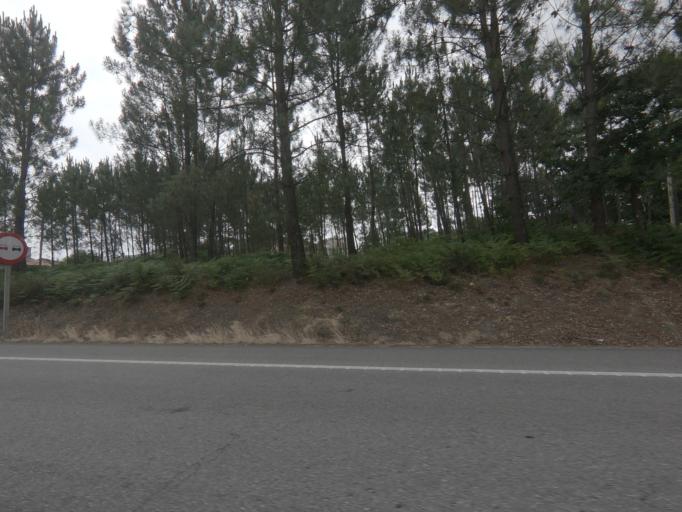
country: PT
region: Viana do Castelo
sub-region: Valenca
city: Valenca
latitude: 41.9997
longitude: -8.6864
